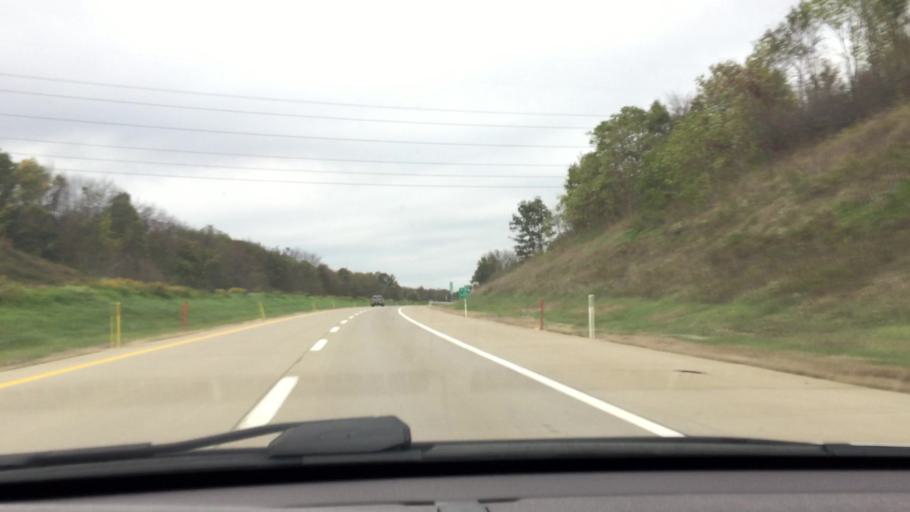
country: US
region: Pennsylvania
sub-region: Beaver County
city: Big Beaver
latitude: 40.8214
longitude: -80.3713
